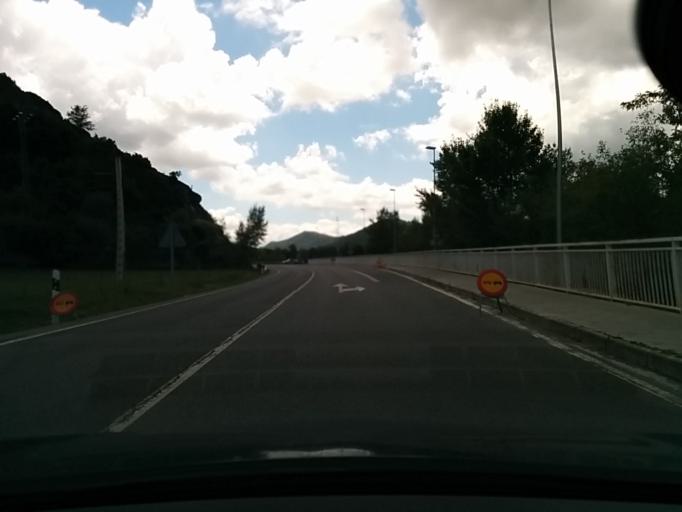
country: ES
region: Aragon
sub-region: Provincia de Huesca
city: Boltana
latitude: 42.4377
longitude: 0.0777
